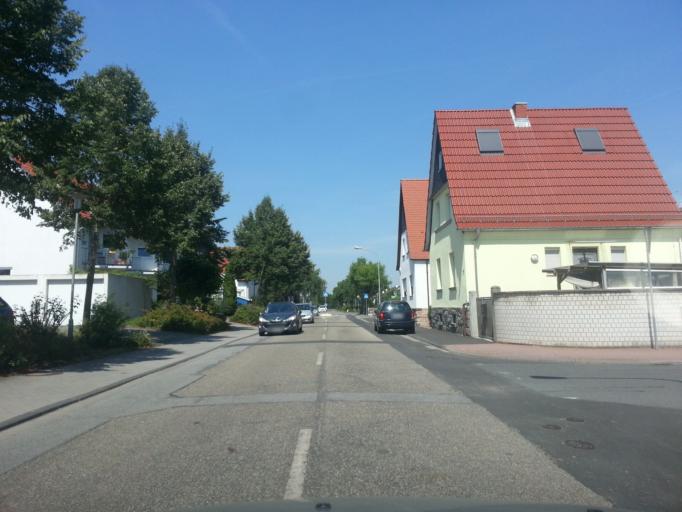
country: DE
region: Hesse
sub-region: Regierungsbezirk Darmstadt
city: Einhausen
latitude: 49.6754
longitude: 8.5401
